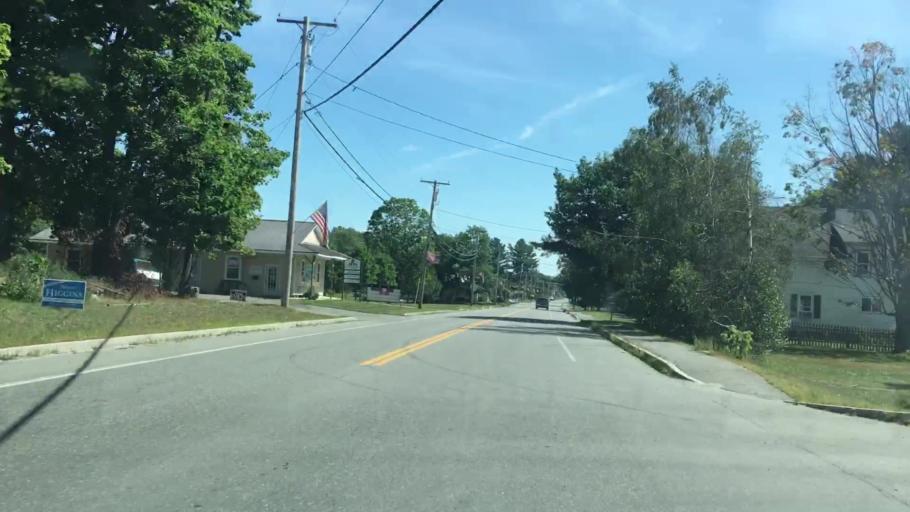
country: US
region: Maine
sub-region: Piscataquis County
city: Milo
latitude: 45.2502
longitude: -68.9819
